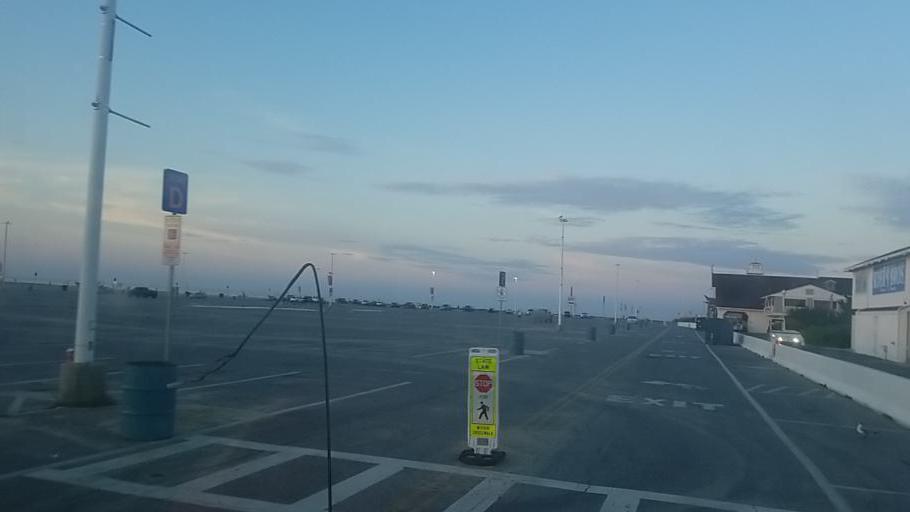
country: US
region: Maryland
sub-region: Worcester County
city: Ocean City
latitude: 38.3262
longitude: -75.0873
